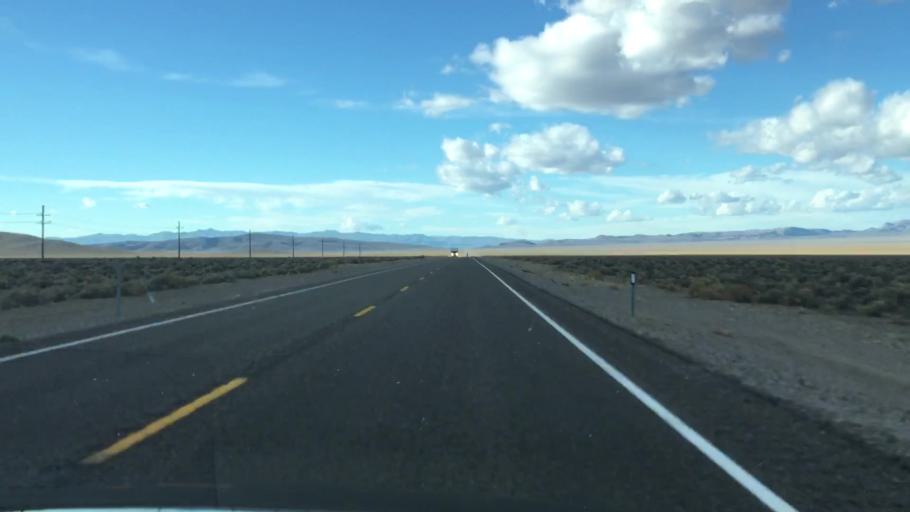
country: US
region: Nevada
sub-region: Nye County
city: Beatty
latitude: 37.1213
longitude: -116.8245
